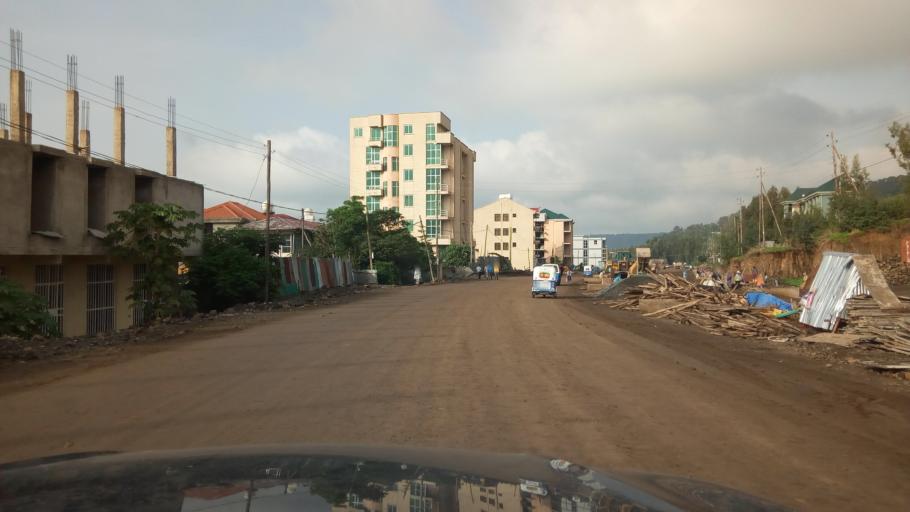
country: ET
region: Amhara
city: Gondar
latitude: 12.5669
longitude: 37.4343
